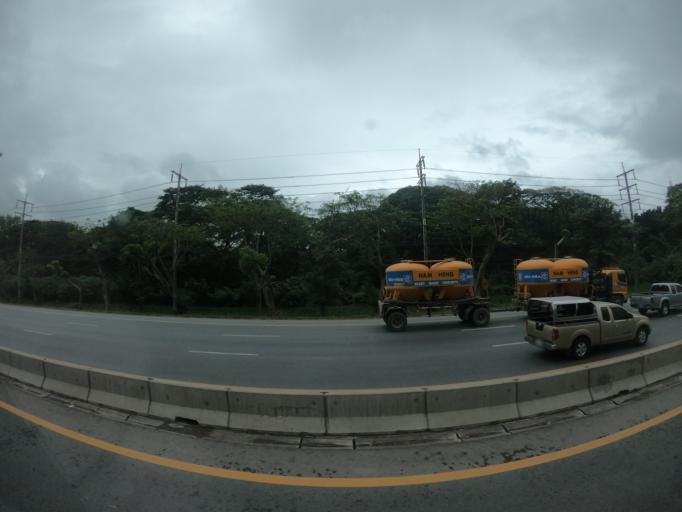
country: TH
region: Sara Buri
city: Kaeng Khoi
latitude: 14.6218
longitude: 101.0897
